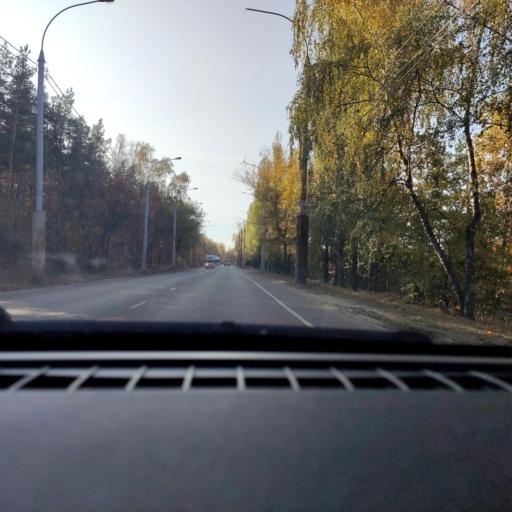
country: RU
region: Voronezj
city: Somovo
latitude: 51.7074
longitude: 39.2915
